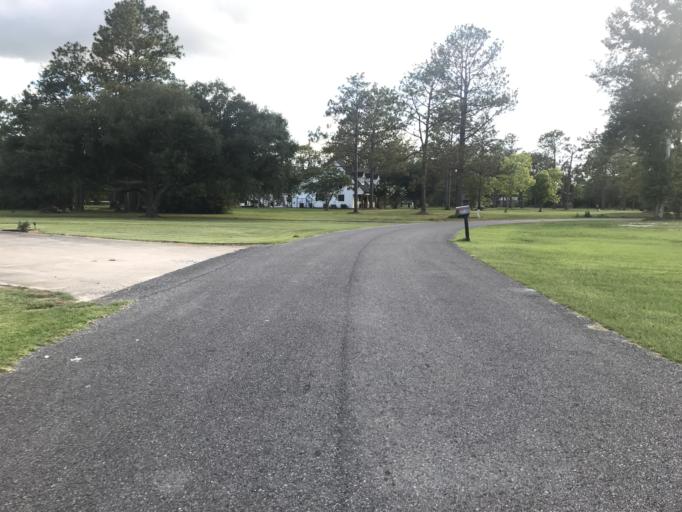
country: US
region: Louisiana
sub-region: Calcasieu Parish
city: Moss Bluff
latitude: 30.3398
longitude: -93.2598
